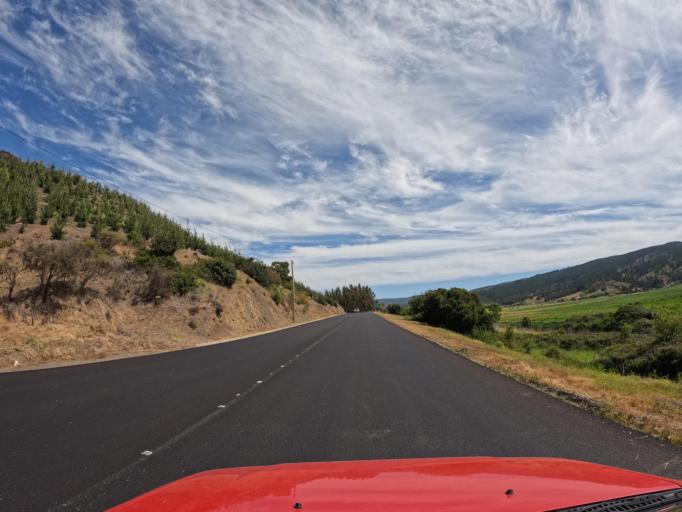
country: CL
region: Maule
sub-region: Provincia de Talca
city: Constitucion
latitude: -35.0507
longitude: -72.0454
